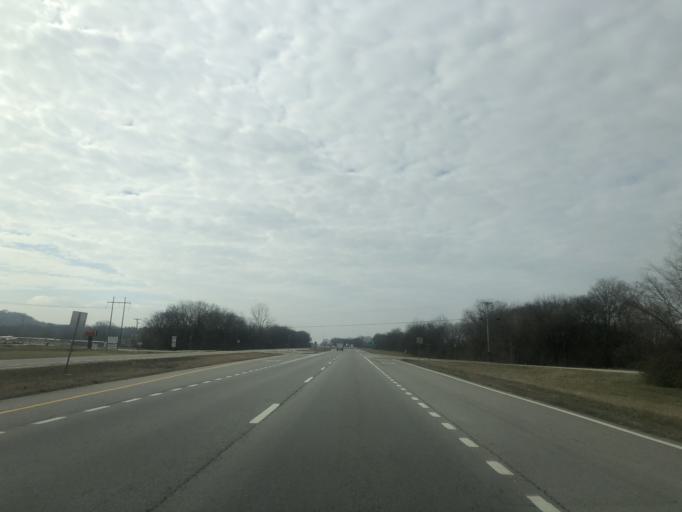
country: US
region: Tennessee
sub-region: Maury County
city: Mount Pleasant
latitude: 35.5522
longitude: -87.2076
